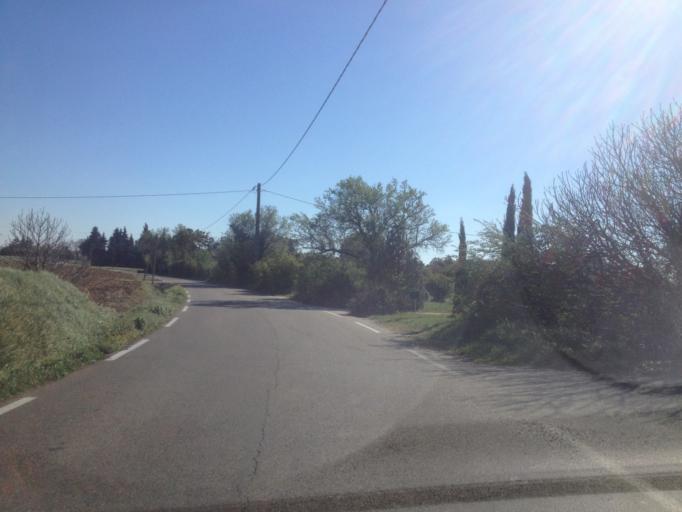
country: FR
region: Provence-Alpes-Cote d'Azur
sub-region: Departement du Vaucluse
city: Orange
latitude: 44.1539
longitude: 4.8251
